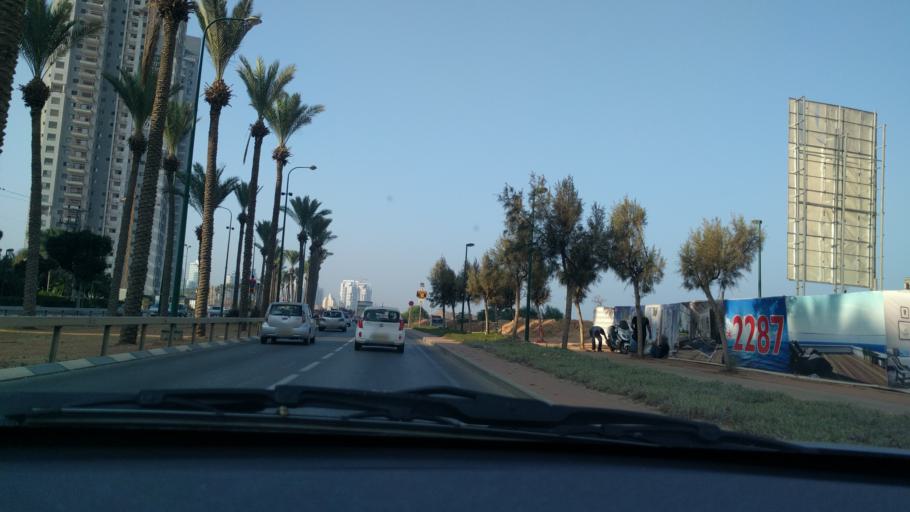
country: IL
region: Central District
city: Netanya
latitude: 32.2948
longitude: 34.8427
